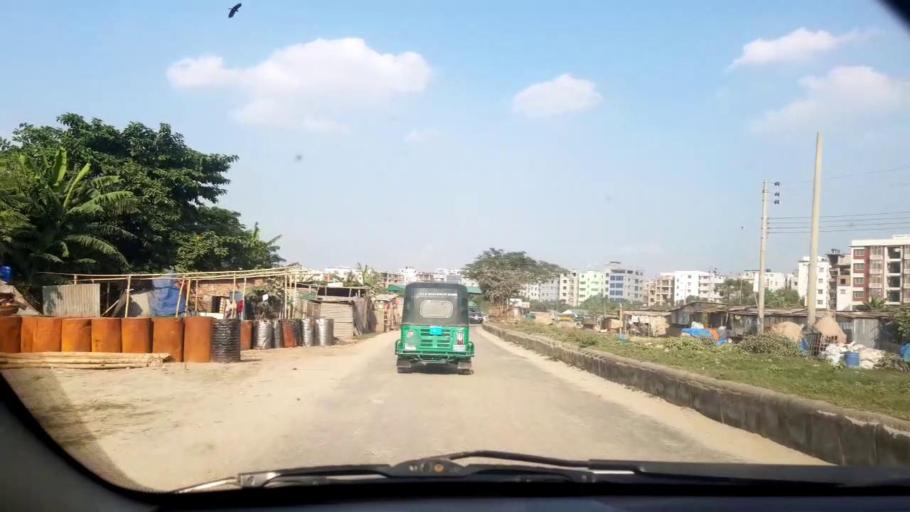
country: BD
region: Dhaka
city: Tungi
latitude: 23.8696
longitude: 90.3771
